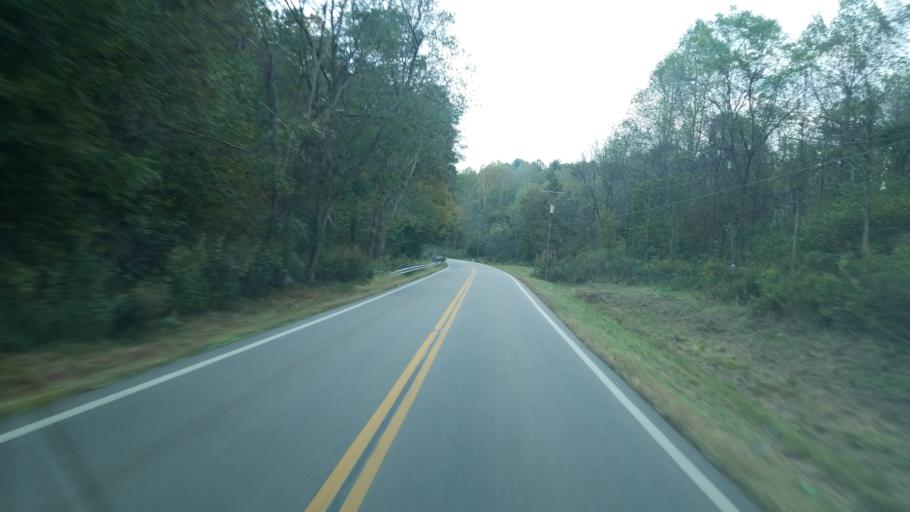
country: US
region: Ohio
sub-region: Meigs County
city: Pomeroy
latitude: 39.1121
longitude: -82.1083
